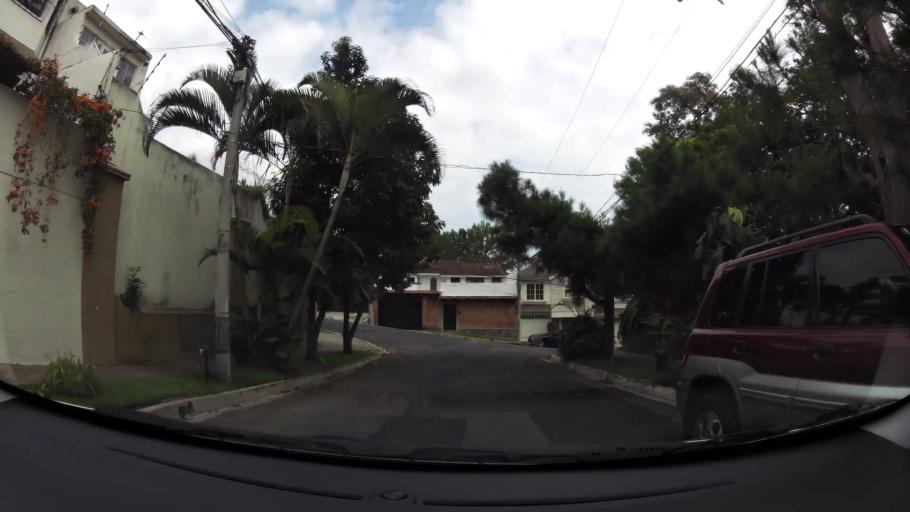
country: SV
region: La Libertad
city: Santa Tecla
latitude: 13.7059
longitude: -89.2608
